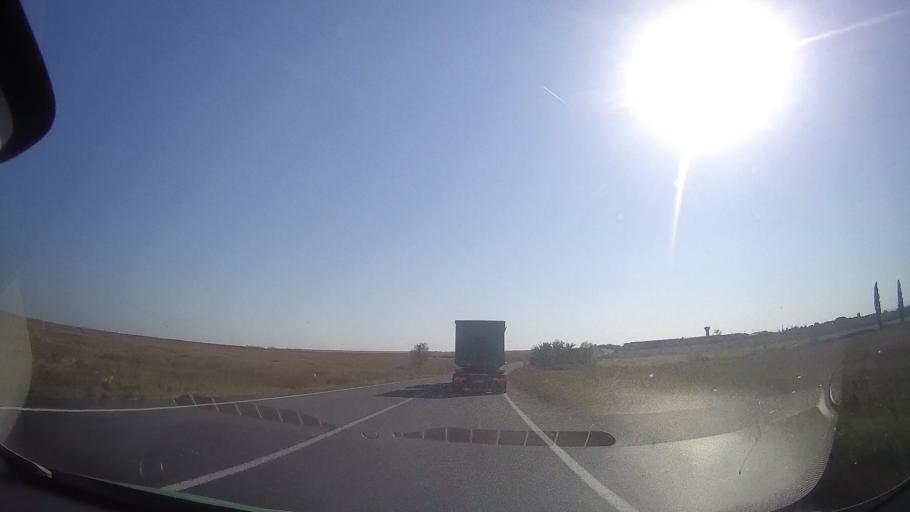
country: RO
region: Timis
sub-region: Comuna Ghizela
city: Ghizela
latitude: 45.7750
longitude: 21.6983
